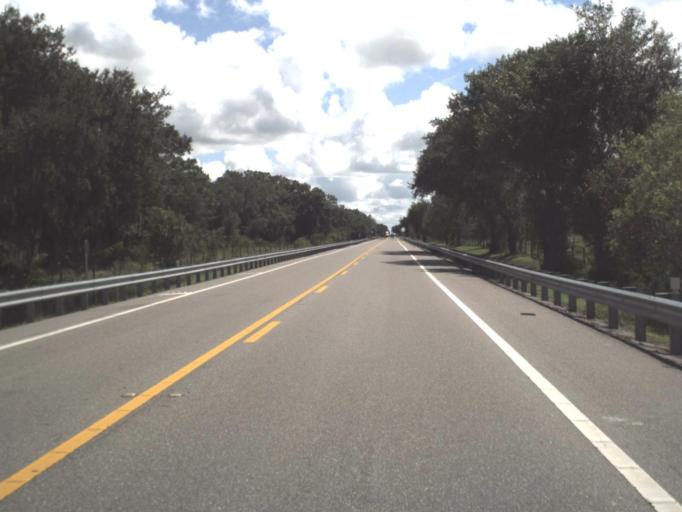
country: US
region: Florida
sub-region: Sarasota County
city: Lake Sarasota
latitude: 27.3798
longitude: -82.2349
